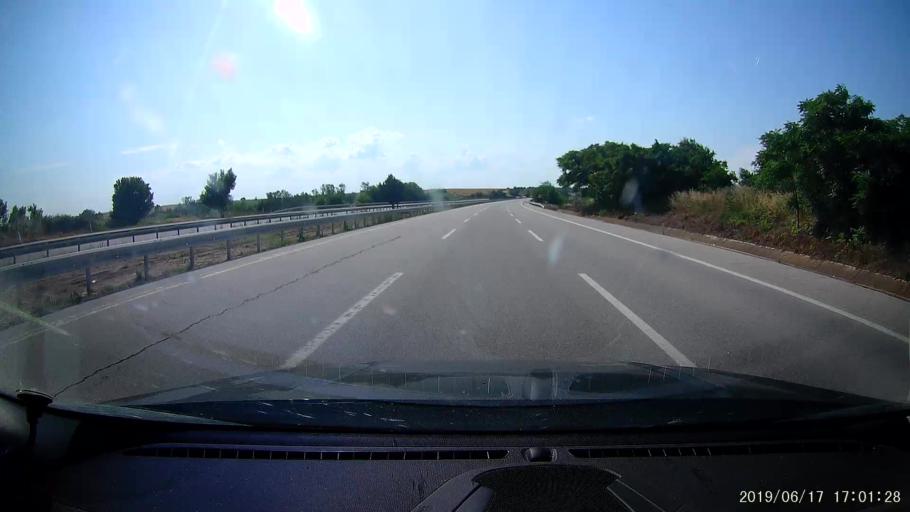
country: TR
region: Edirne
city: Haskoy
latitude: 41.6289
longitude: 26.8041
